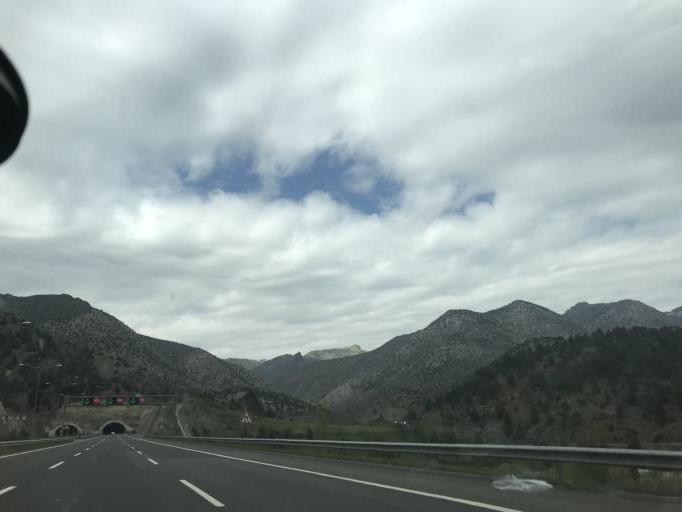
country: TR
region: Nigde
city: Ciftehan
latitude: 37.5177
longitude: 34.8177
